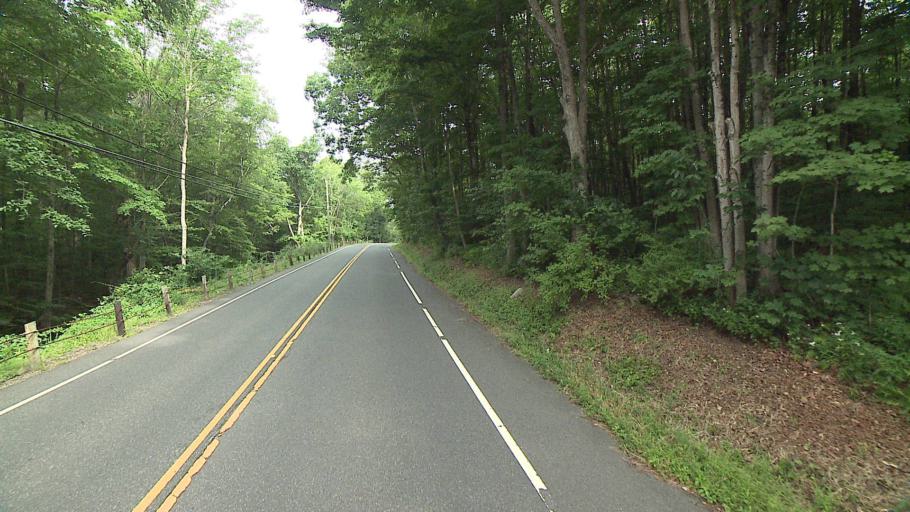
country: US
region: Connecticut
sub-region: Litchfield County
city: Woodbury
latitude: 41.5924
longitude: -73.2557
